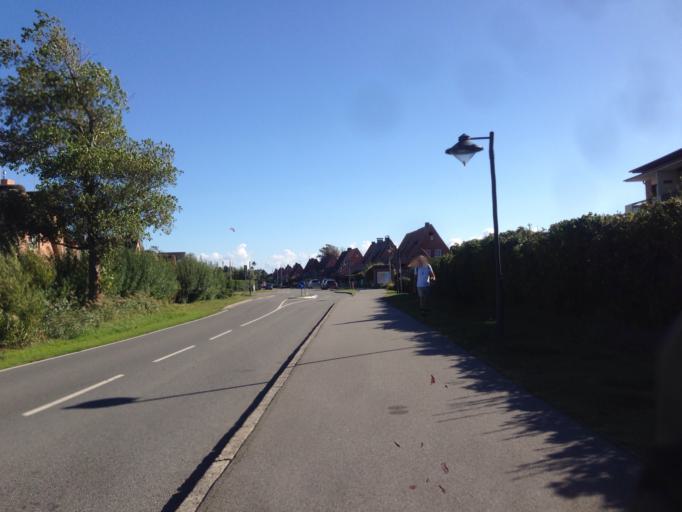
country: DE
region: Schleswig-Holstein
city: List
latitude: 55.0245
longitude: 8.4187
